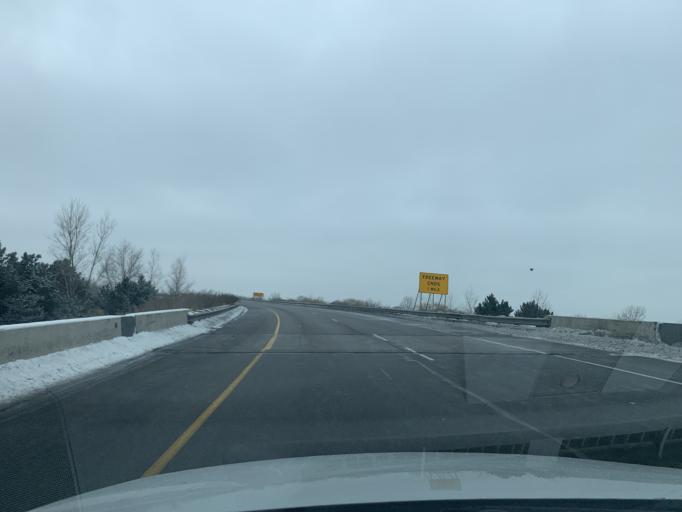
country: US
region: Minnesota
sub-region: Anoka County
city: Coon Rapids
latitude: 45.1224
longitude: -93.3068
